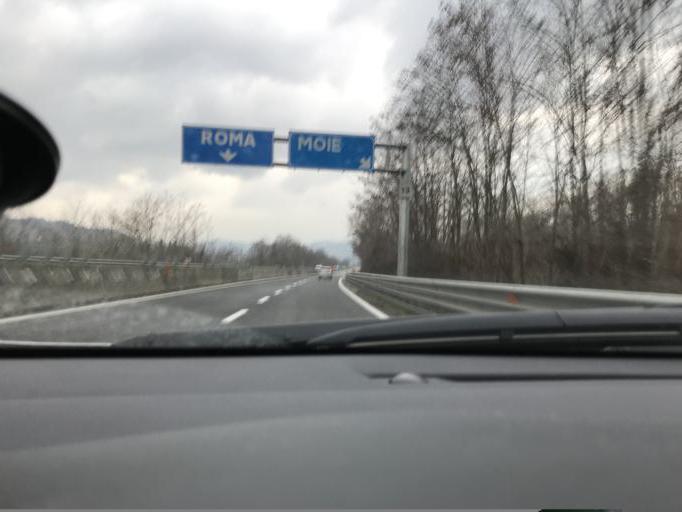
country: IT
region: The Marches
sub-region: Provincia di Ancona
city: Moie
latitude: 43.4949
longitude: 13.1317
